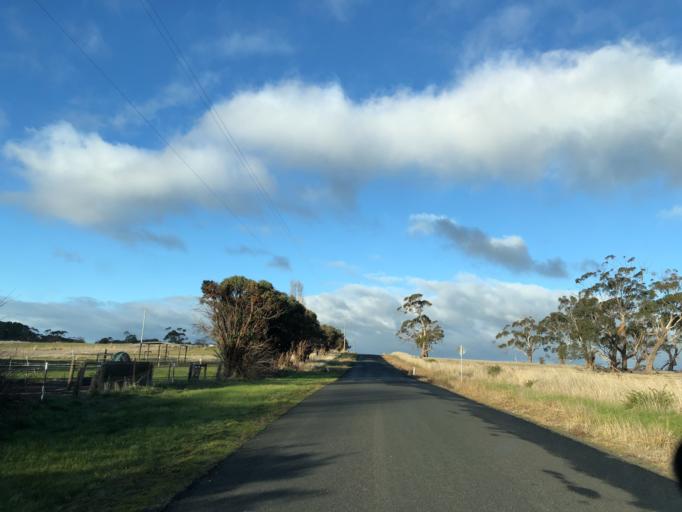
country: AU
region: Victoria
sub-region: Mount Alexander
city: Castlemaine
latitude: -37.2134
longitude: 144.3345
